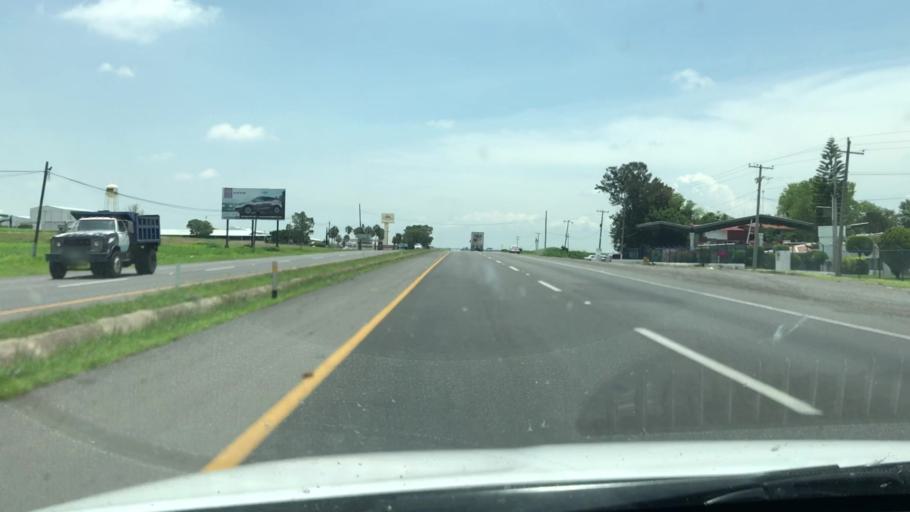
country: MX
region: Guanajuato
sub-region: Penjamo
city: Mezquite de Luna
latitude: 20.3805
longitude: -101.8251
